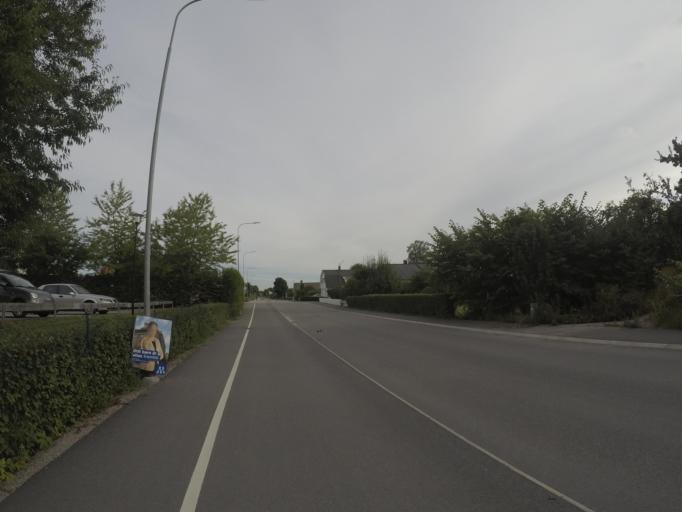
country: SE
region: OErebro
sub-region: Orebro Kommun
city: Orebro
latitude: 59.2570
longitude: 15.2486
